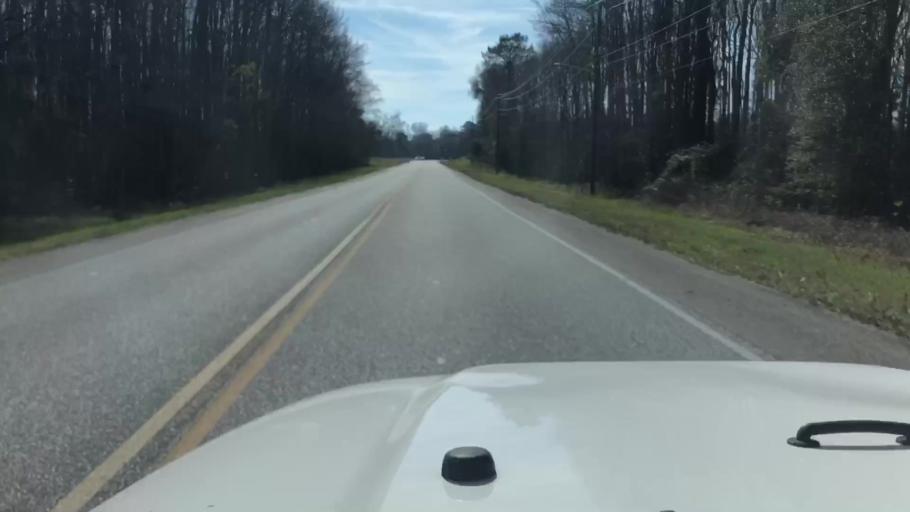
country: US
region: Alabama
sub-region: Elmore County
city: Blue Ridge
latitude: 32.4017
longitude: -86.1663
